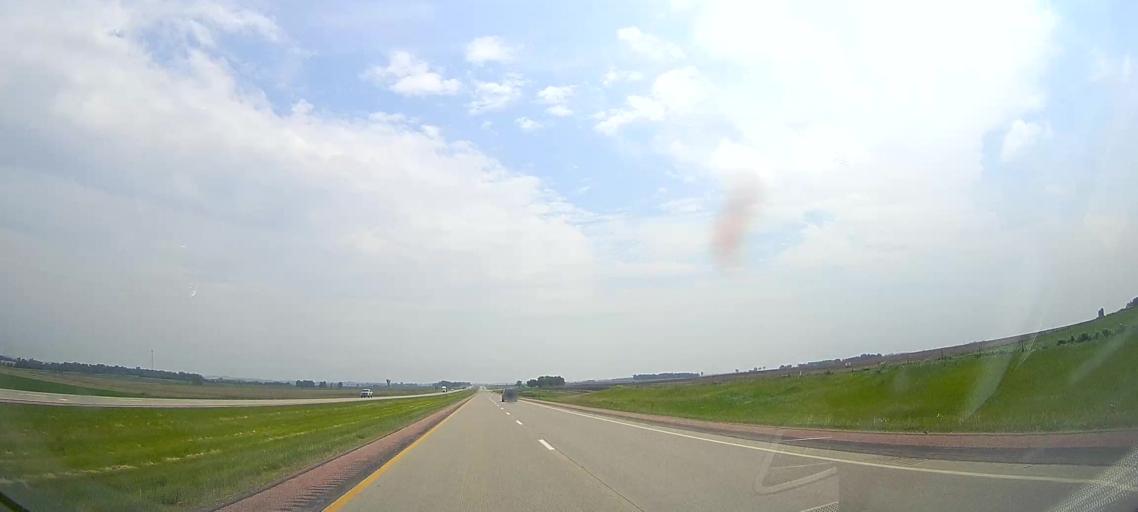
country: US
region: South Dakota
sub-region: Union County
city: Beresford
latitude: 42.9978
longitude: -96.7958
